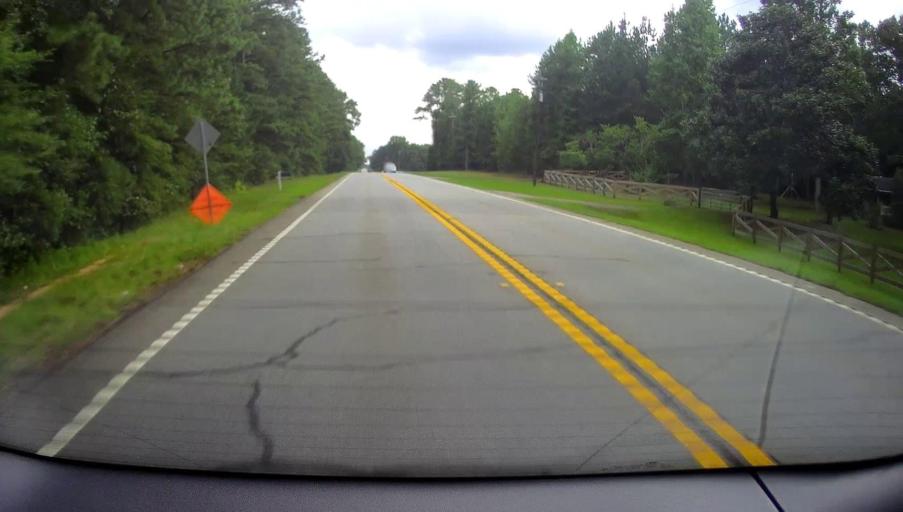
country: US
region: Georgia
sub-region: Coweta County
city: Senoia
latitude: 33.2111
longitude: -84.5804
